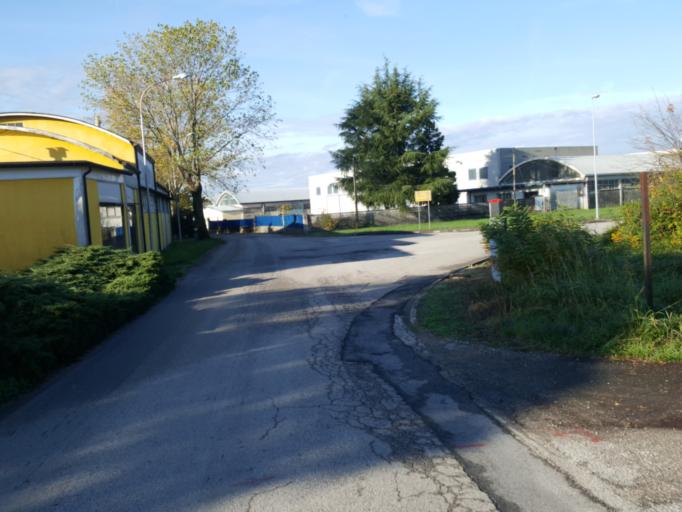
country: IT
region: Friuli Venezia Giulia
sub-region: Provincia di Udine
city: Manzano
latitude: 45.9864
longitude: 13.3673
